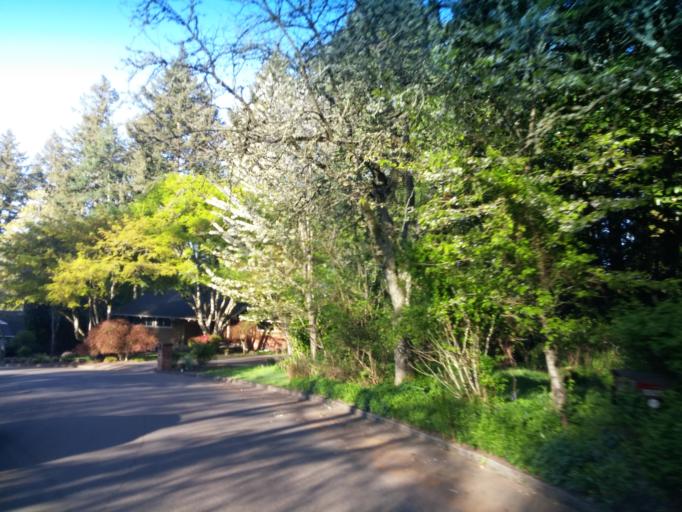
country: US
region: Oregon
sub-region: Washington County
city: Cedar Hills
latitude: 45.5121
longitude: -122.7938
